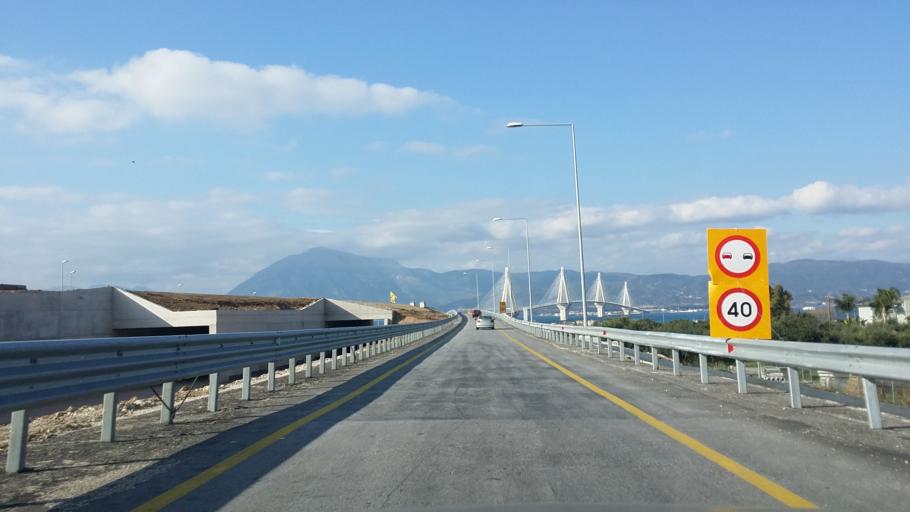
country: GR
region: West Greece
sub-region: Nomos Achaias
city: Rio
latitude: 38.2996
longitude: 21.7927
